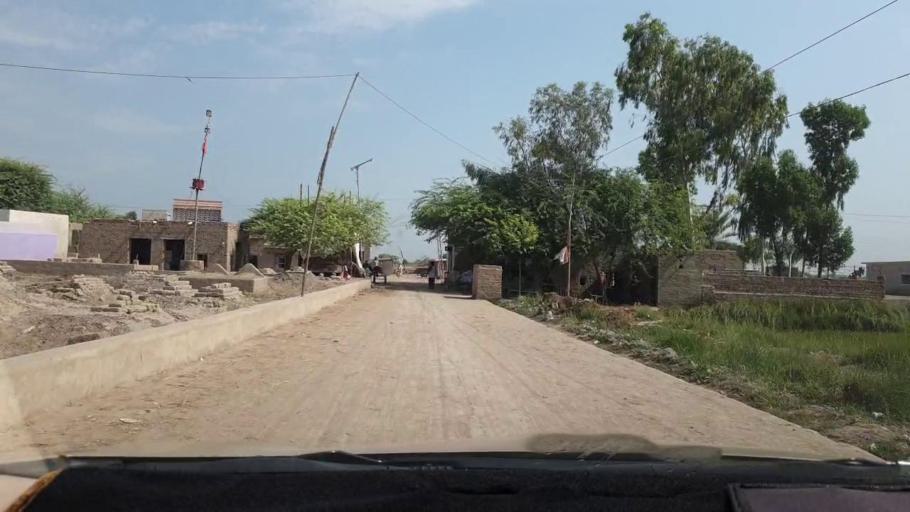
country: PK
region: Sindh
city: Larkana
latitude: 27.6669
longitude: 68.2228
